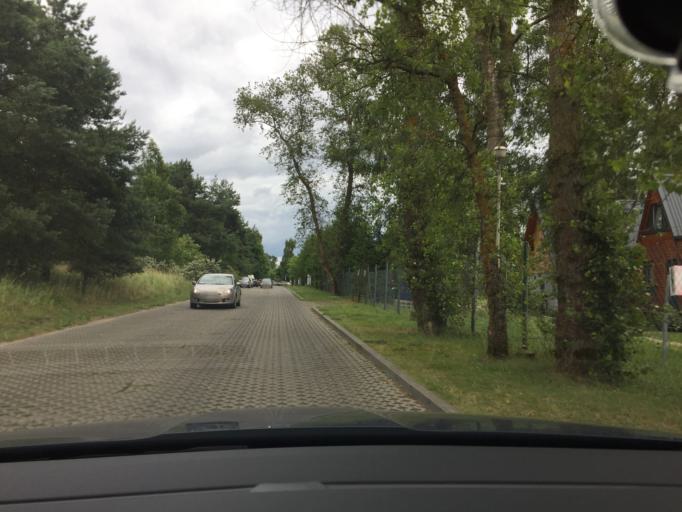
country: PL
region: Pomeranian Voivodeship
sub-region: Gdansk
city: Gdansk
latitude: 54.3683
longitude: 18.7730
